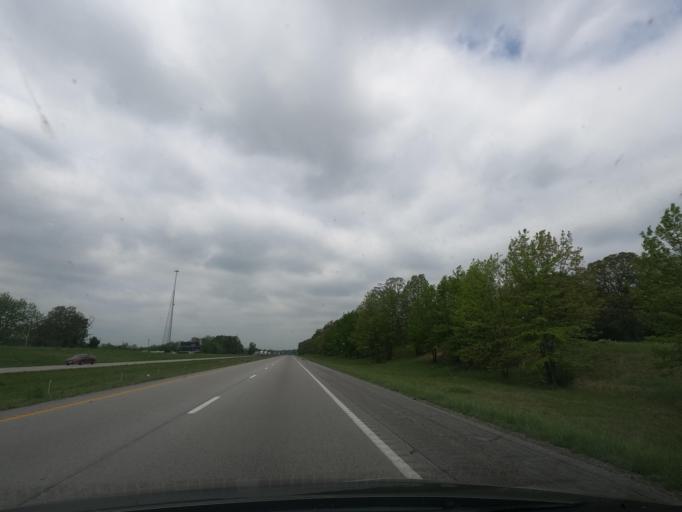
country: US
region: Missouri
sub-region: Jasper County
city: Duenweg
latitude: 37.0823
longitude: -94.3512
